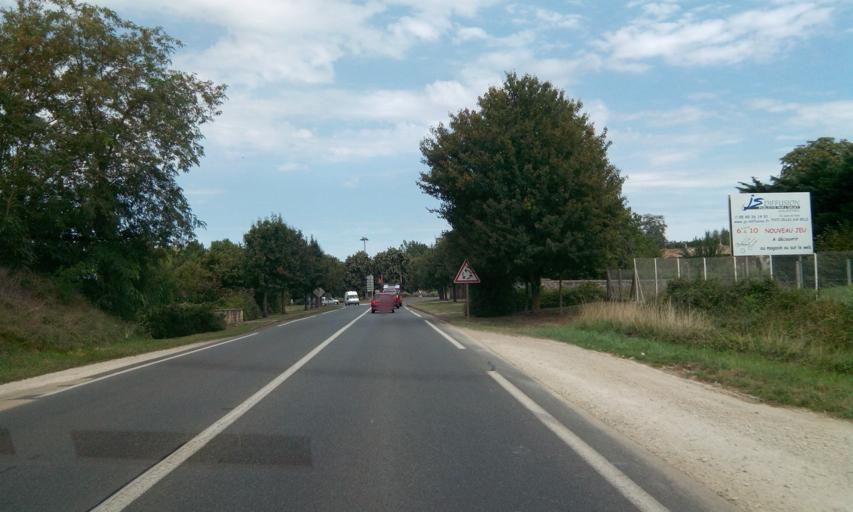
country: FR
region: Poitou-Charentes
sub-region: Departement des Deux-Sevres
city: Melle
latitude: 46.2230
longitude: -0.1551
